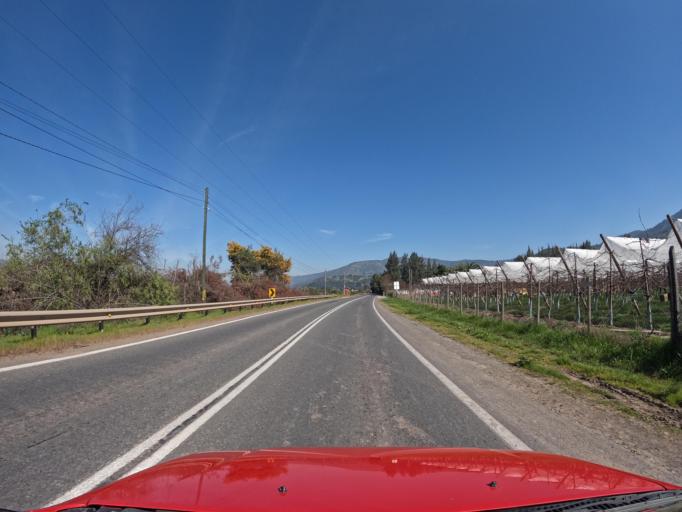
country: CL
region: Maule
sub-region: Provincia de Curico
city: Rauco
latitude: -34.9808
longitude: -71.4074
